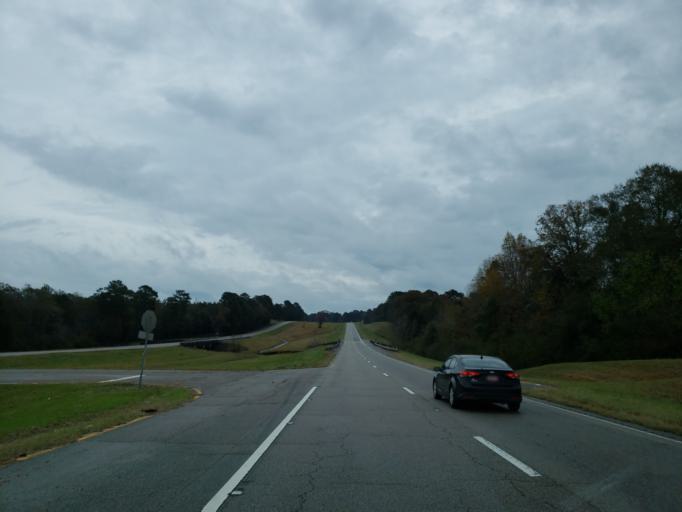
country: US
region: Mississippi
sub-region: Jones County
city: Sharon
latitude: 31.7001
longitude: -88.9022
